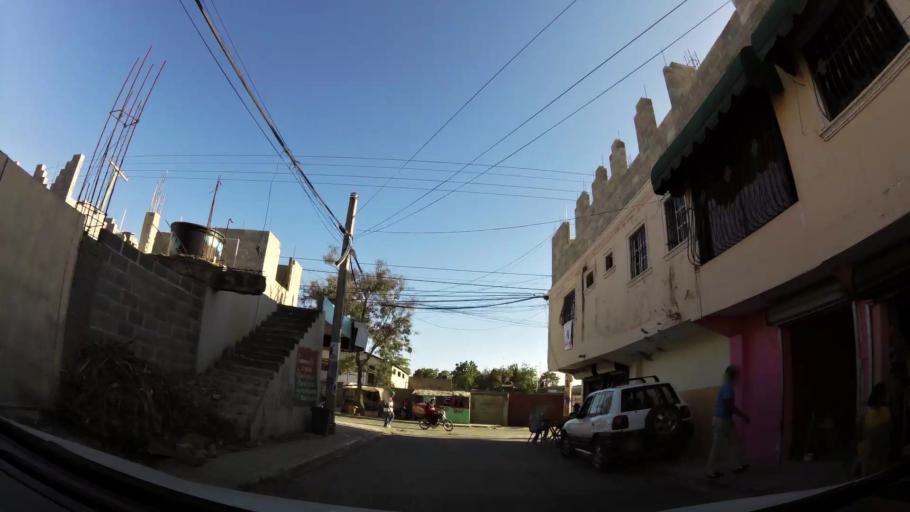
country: DO
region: Santo Domingo
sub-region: Santo Domingo
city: Santo Domingo Este
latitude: 18.4811
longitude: -69.8167
